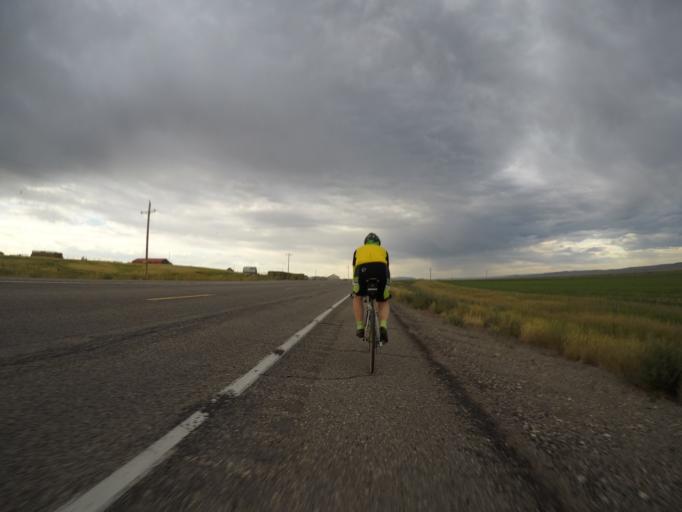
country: US
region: Utah
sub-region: Rich County
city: Randolph
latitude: 41.9550
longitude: -110.9482
